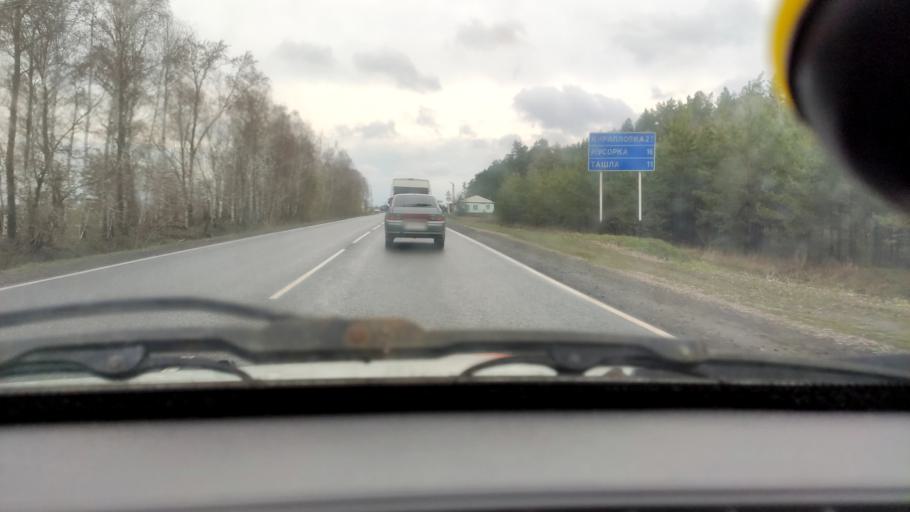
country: RU
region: Samara
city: Povolzhskiy
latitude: 53.6275
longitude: 49.6545
